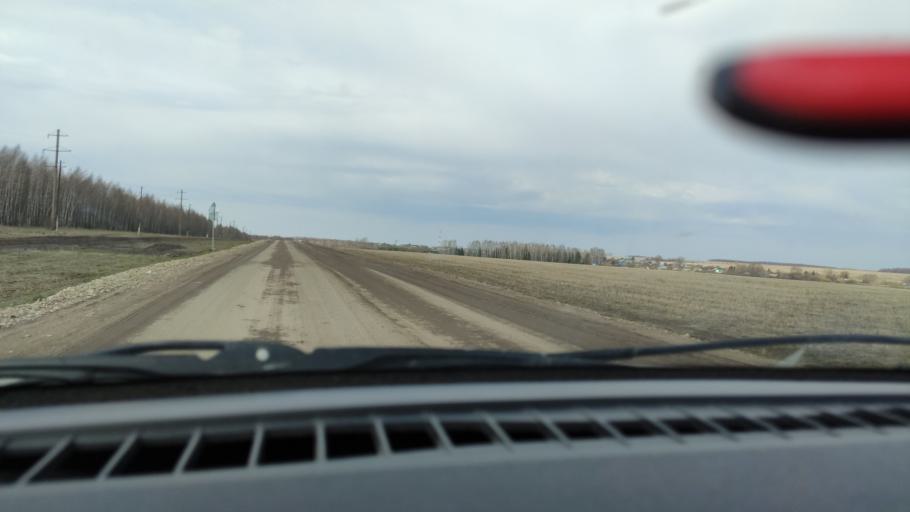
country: RU
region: Bashkortostan
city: Burayevo
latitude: 55.6576
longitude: 55.1519
